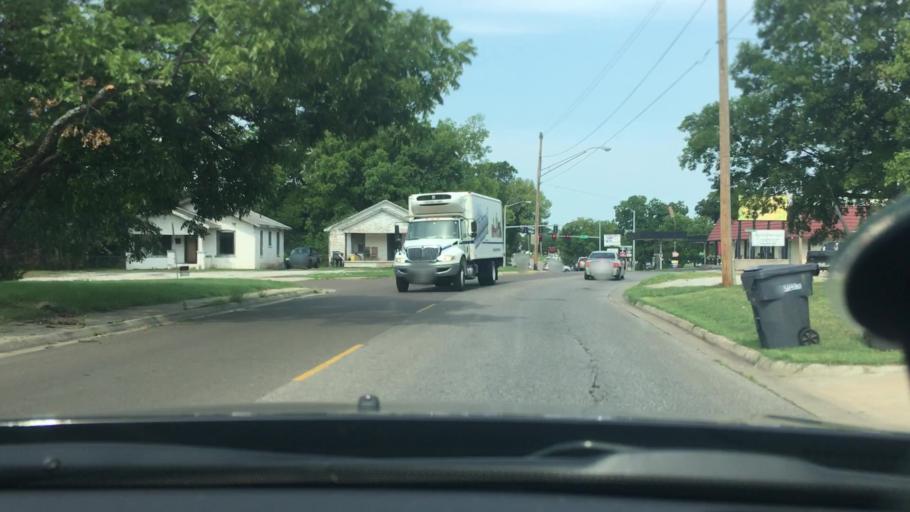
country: US
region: Oklahoma
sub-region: Carter County
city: Ardmore
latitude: 34.1866
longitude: -97.1363
